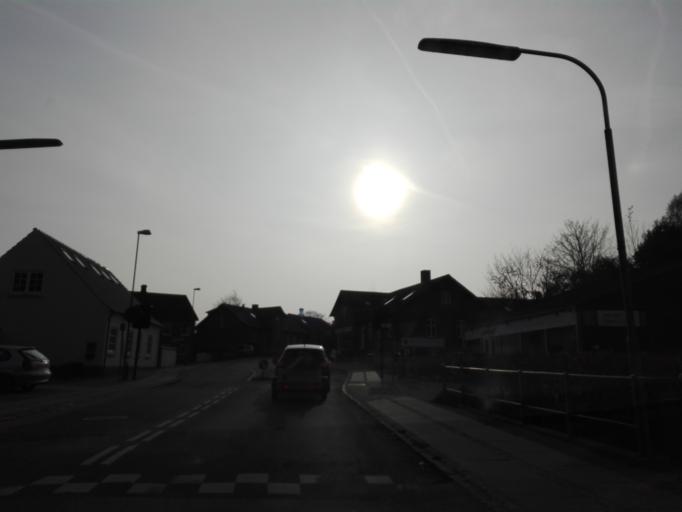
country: DK
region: Central Jutland
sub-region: Arhus Kommune
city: Marslet
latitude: 56.0671
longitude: 10.1611
